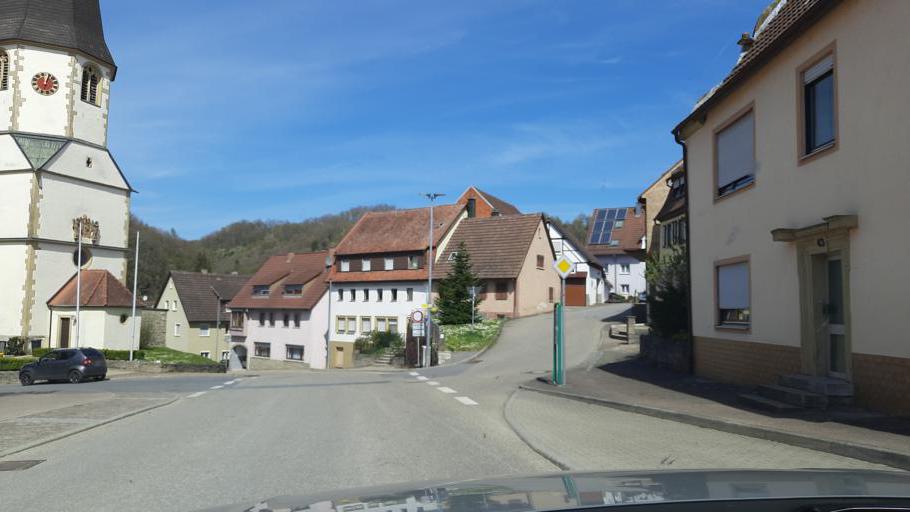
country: DE
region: Baden-Wuerttemberg
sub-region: Regierungsbezirk Stuttgart
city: Jagsthausen
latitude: 49.3269
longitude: 9.4872
